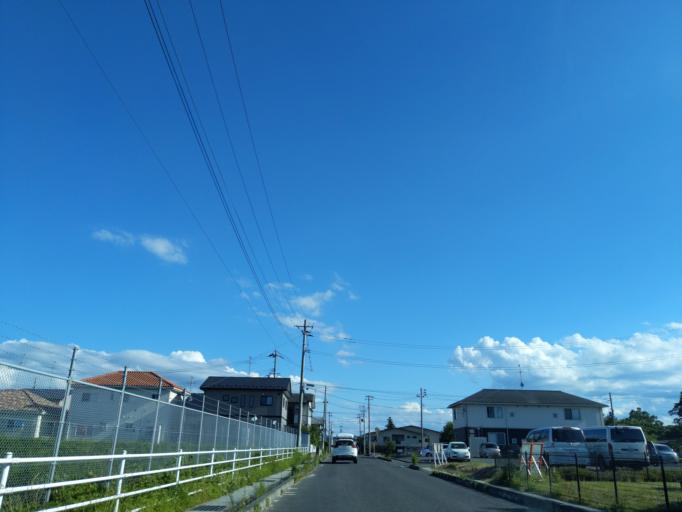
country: JP
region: Fukushima
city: Koriyama
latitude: 37.3842
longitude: 140.3348
